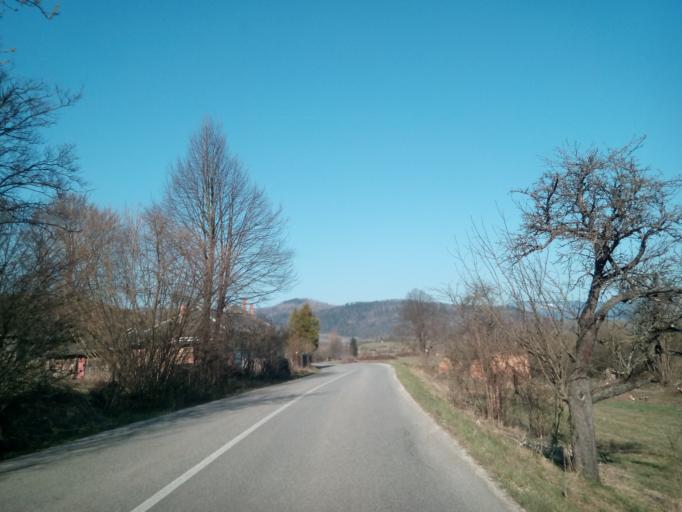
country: SK
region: Kosicky
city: Dobsina
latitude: 48.6777
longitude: 20.3473
